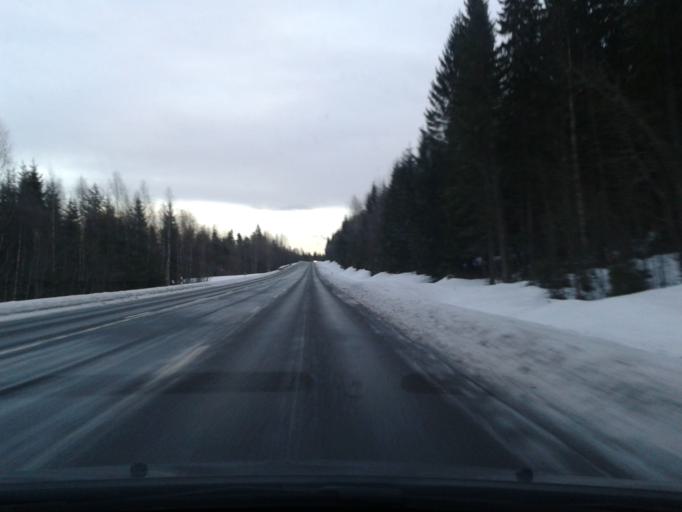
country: SE
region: Vaesternorrland
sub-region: Solleftea Kommun
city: Solleftea
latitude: 63.1350
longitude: 17.4557
